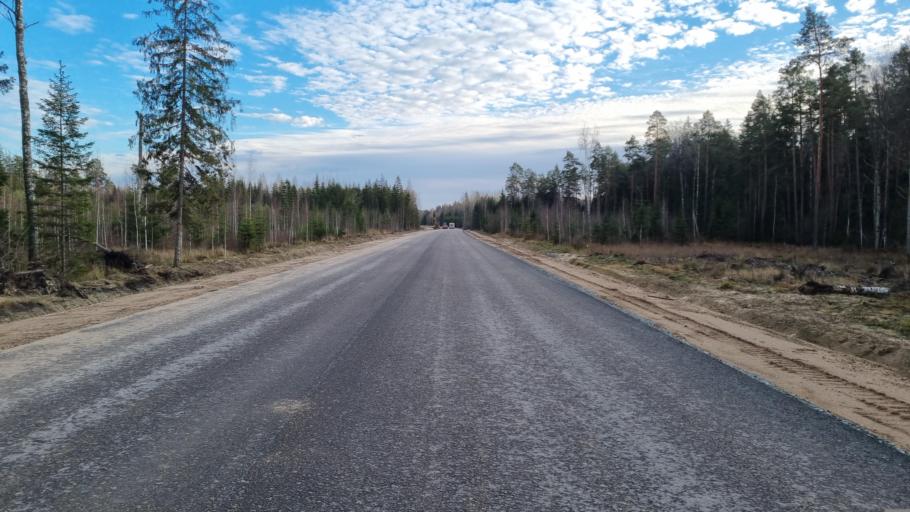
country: LV
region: Kekava
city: Kekava
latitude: 56.7971
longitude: 24.2083
